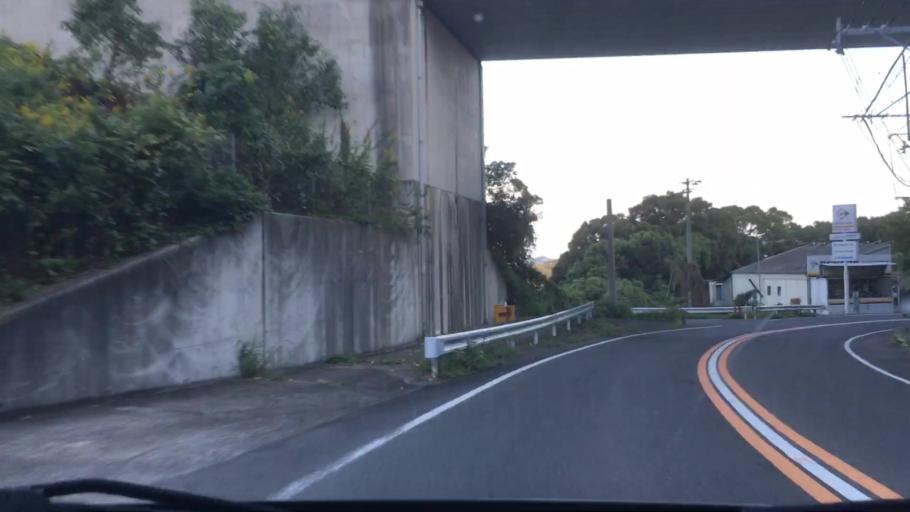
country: JP
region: Nagasaki
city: Sasebo
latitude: 33.0379
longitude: 129.7444
